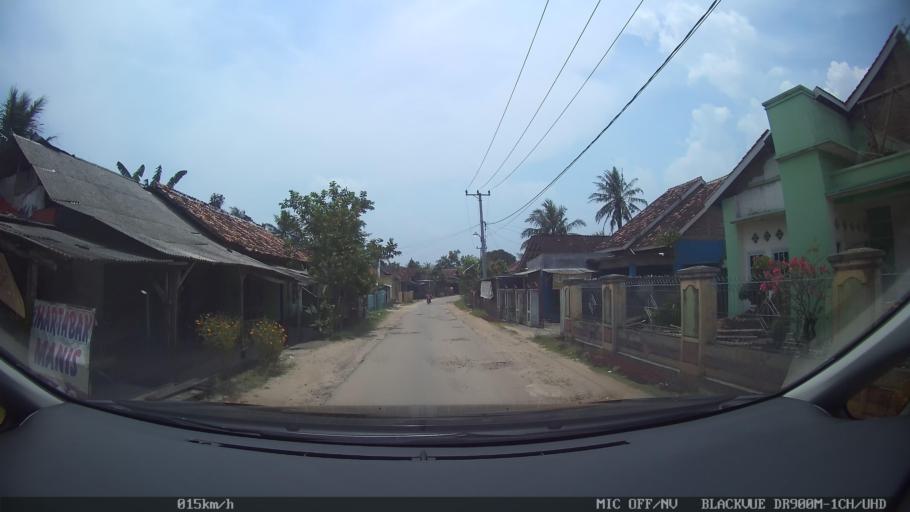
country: ID
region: Lampung
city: Kedaton
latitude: -5.3287
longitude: 105.2492
